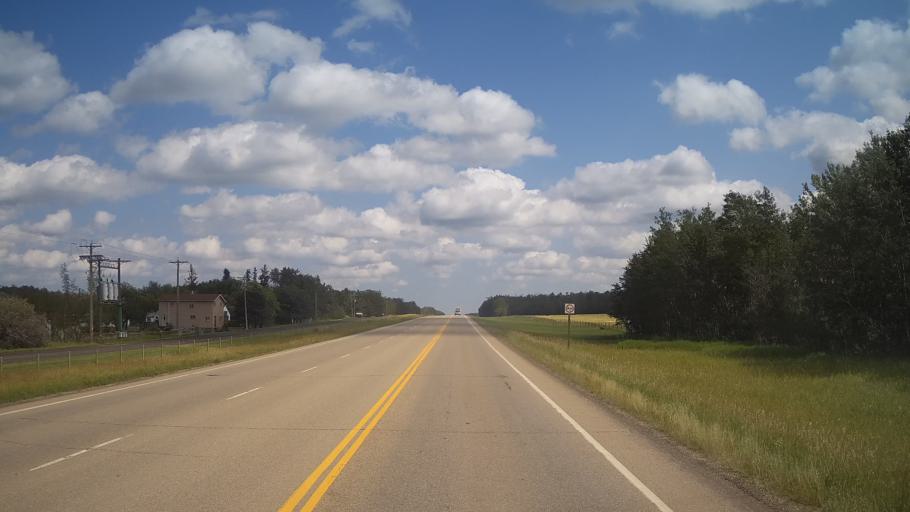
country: CA
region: Alberta
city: Sherwood Park
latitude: 53.3957
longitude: -113.0634
